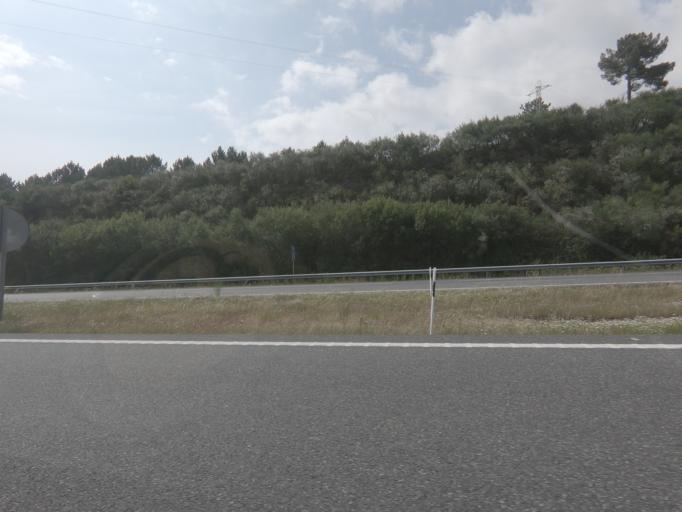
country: ES
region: Galicia
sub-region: Provincia de Ourense
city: Melon
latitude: 42.2128
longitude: -8.2617
